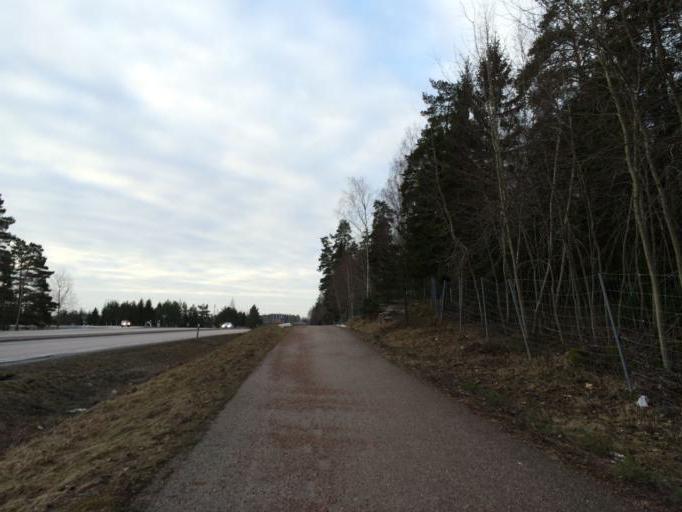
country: SE
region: Vaestmanland
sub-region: Hallstahammars Kommun
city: Hallstahammar
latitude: 59.5958
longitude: 16.2489
